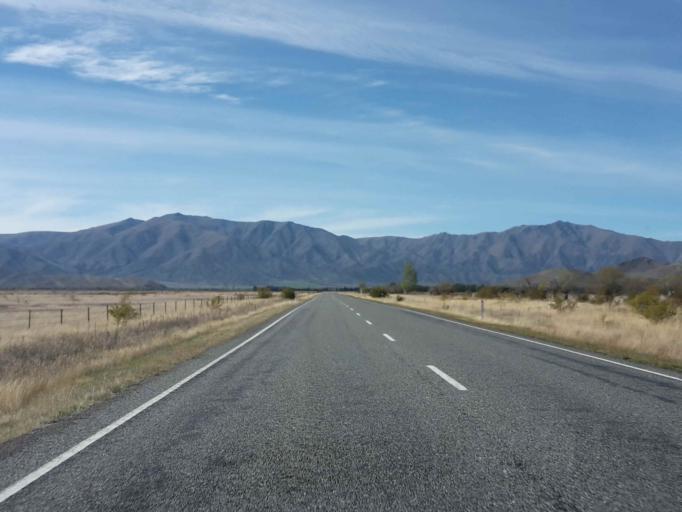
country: NZ
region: Otago
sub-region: Queenstown-Lakes District
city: Wanaka
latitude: -44.4991
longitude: 169.9049
